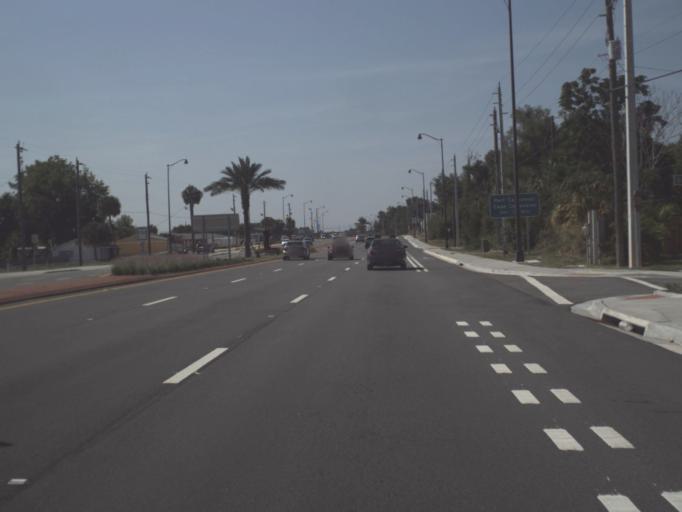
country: US
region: Florida
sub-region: Brevard County
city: Cocoa
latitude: 28.3922
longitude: -80.7475
